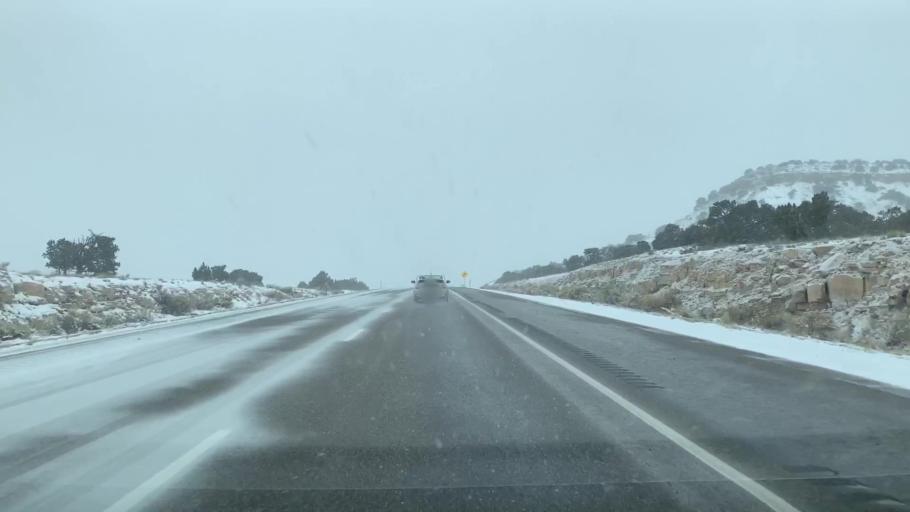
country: US
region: Utah
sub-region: Emery County
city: Castle Dale
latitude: 38.9081
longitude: -110.5299
